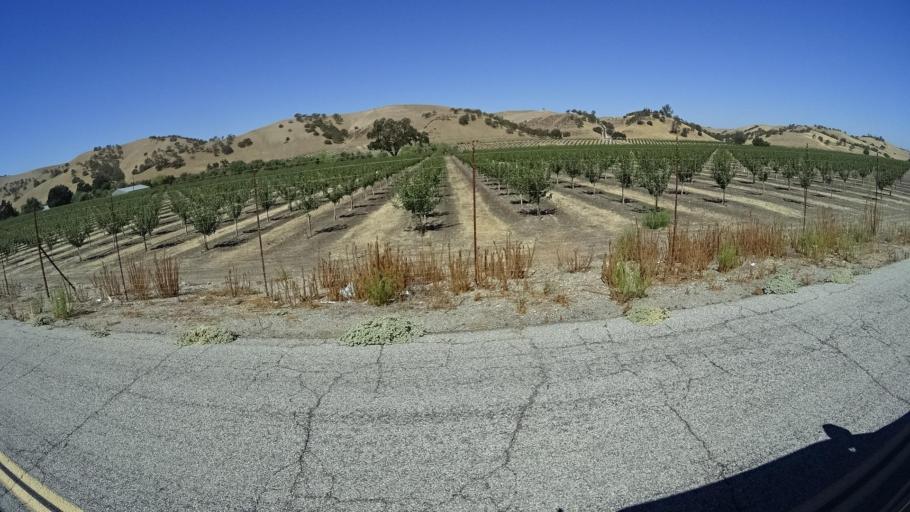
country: US
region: California
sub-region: San Luis Obispo County
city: San Miguel
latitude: 35.8108
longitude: -120.6675
